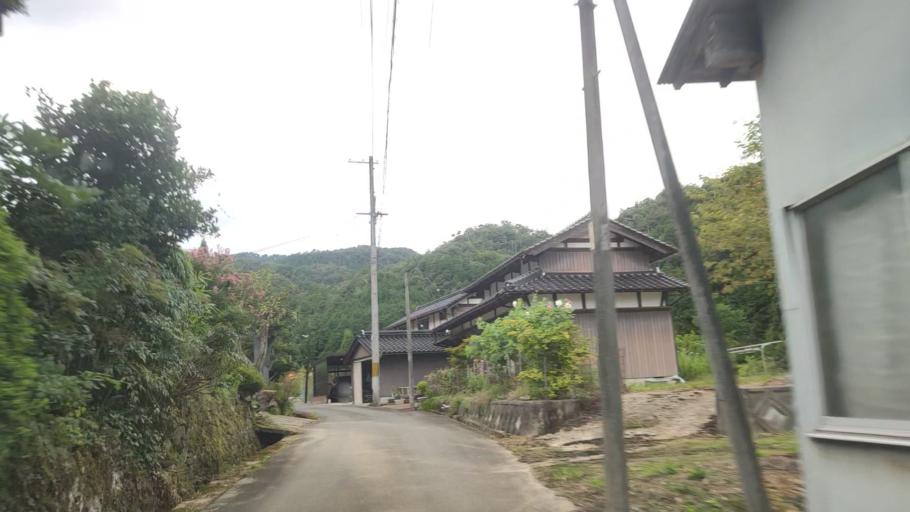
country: JP
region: Hyogo
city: Toyooka
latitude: 35.6010
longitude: 134.8789
